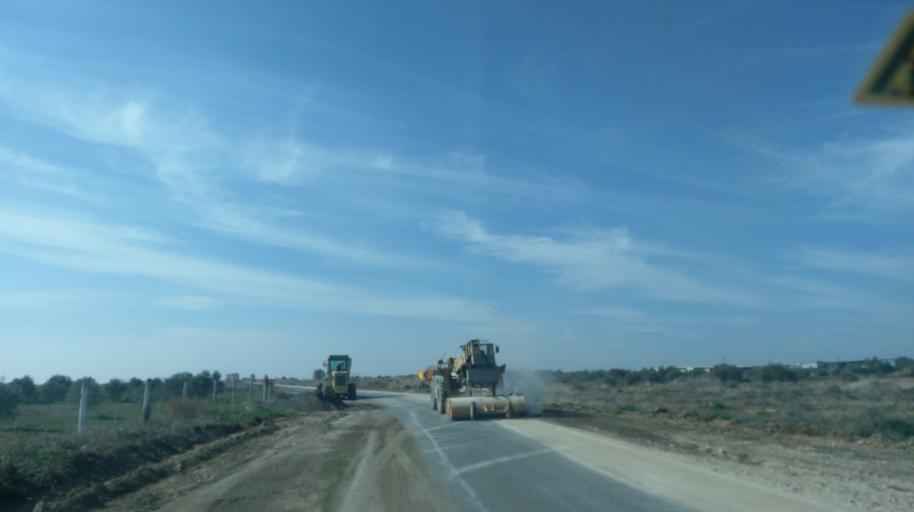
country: CY
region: Larnaka
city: Pergamos
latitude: 35.1516
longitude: 33.6844
